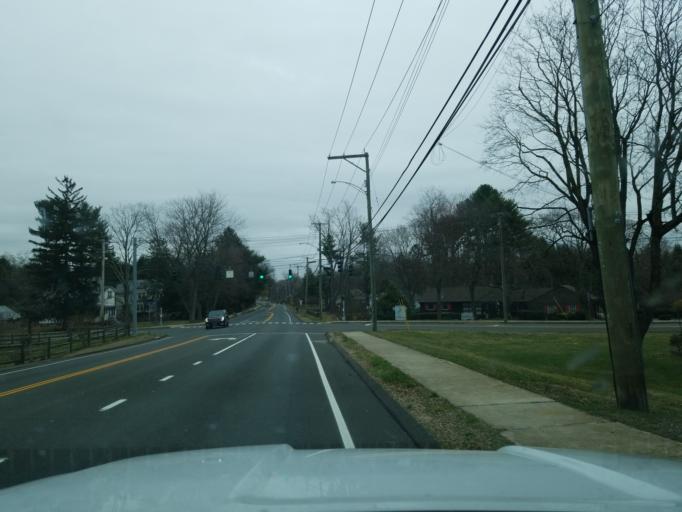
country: US
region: Connecticut
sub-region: New Haven County
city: North Haven
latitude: 41.3892
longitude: -72.8557
